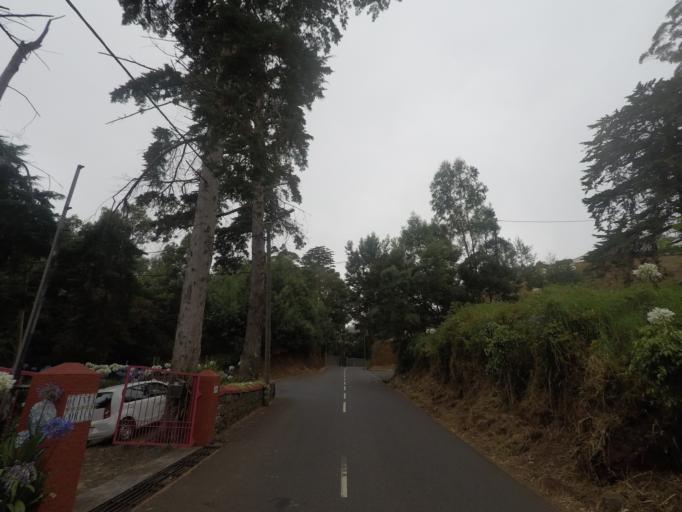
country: PT
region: Madeira
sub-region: Funchal
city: Nossa Senhora do Monte
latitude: 32.6676
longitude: -16.8787
